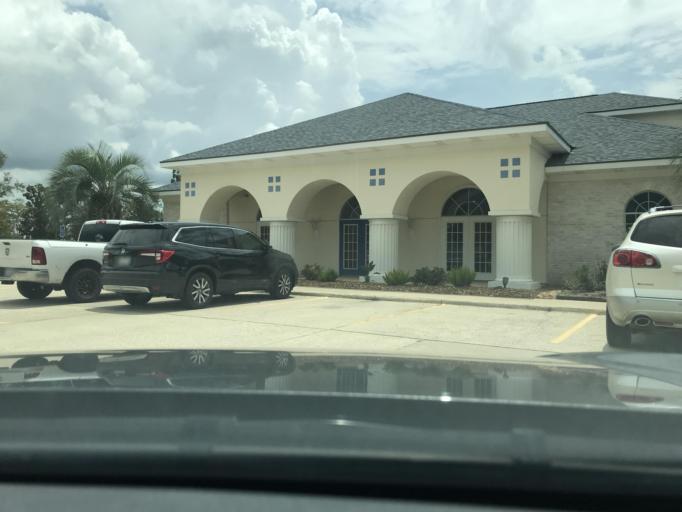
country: US
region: Louisiana
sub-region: Calcasieu Parish
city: Sulphur
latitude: 30.2274
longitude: -93.3407
